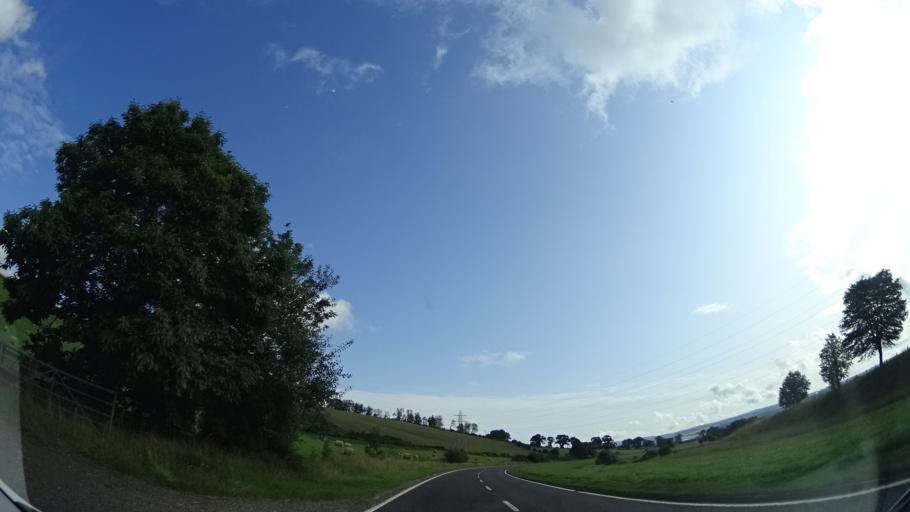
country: GB
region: Scotland
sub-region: Highland
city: Conon Bridge
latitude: 57.5779
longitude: -4.4466
